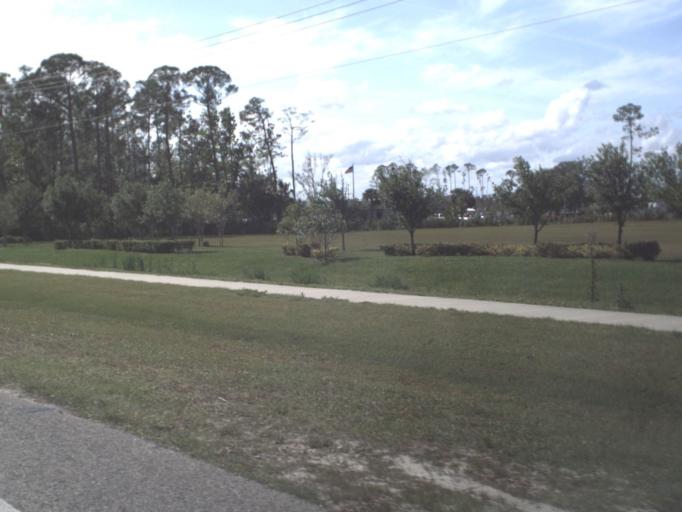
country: US
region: Florida
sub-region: Flagler County
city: Flagler Beach
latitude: 29.4758
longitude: -81.1900
